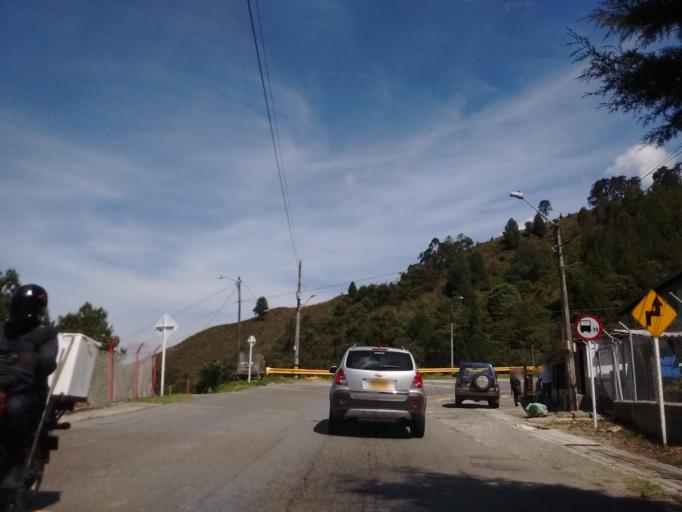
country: CO
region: Antioquia
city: Medellin
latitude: 6.2425
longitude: -75.5177
